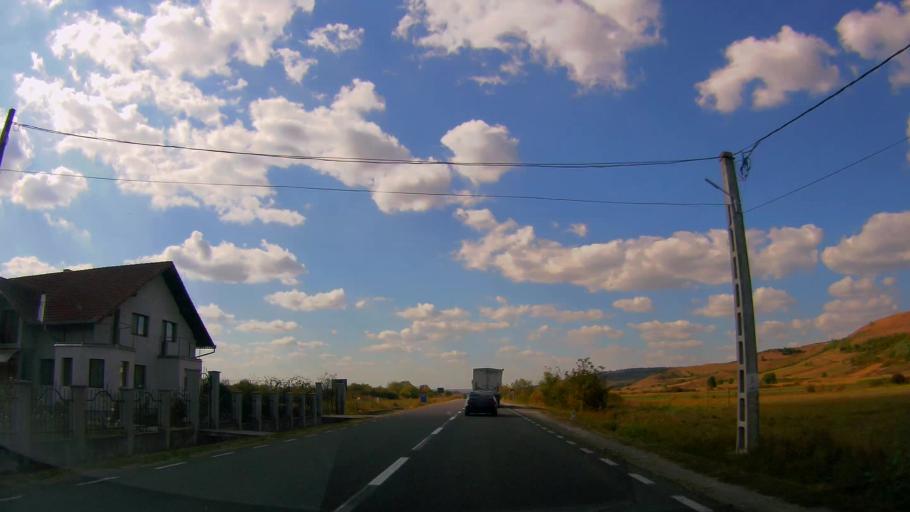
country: RO
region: Salaj
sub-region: Comuna Bocsa
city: Bocsa
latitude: 47.3199
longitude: 22.8969
